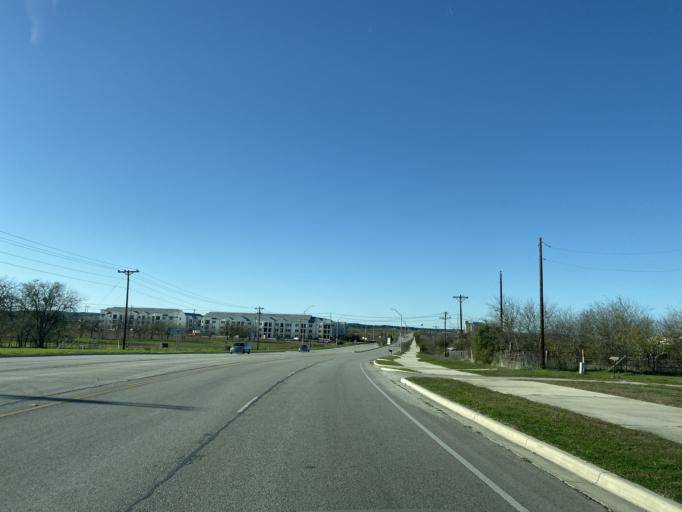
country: US
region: Texas
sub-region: Guadalupe County
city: Redwood
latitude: 29.8287
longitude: -97.9593
